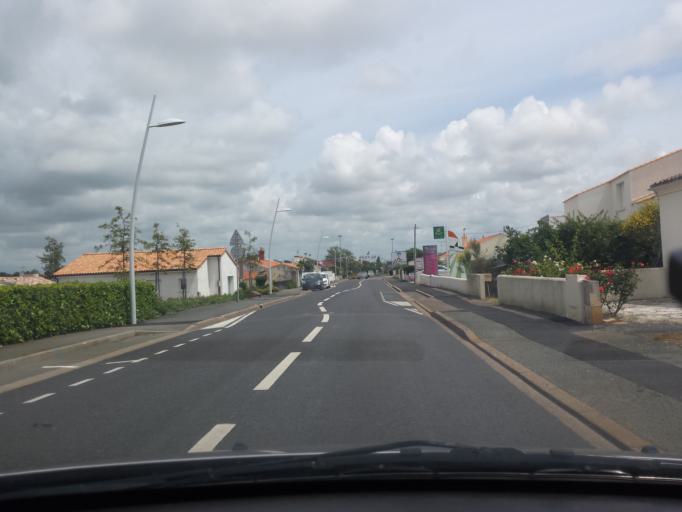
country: FR
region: Pays de la Loire
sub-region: Departement de la Vendee
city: Saint-Hilaire-de-Riez
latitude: 46.6948
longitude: -1.9179
